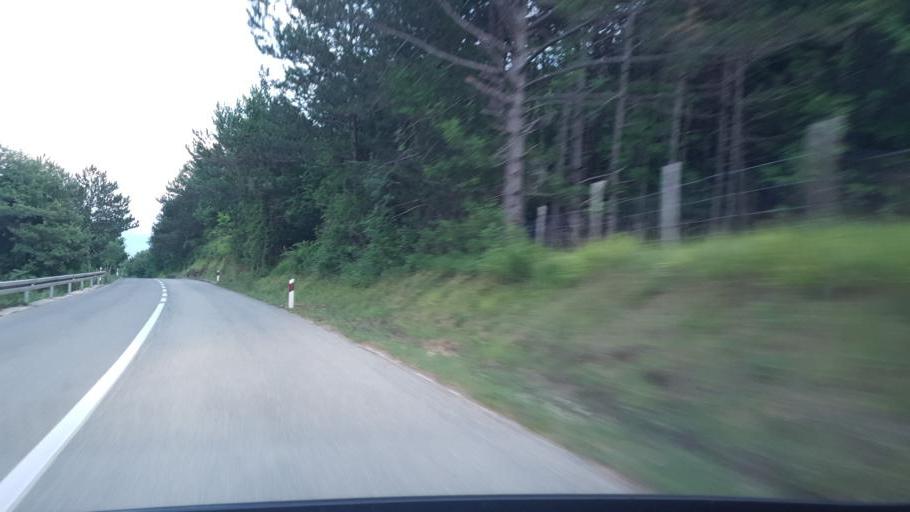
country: HR
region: Primorsko-Goranska
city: Punat
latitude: 45.0061
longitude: 14.7028
